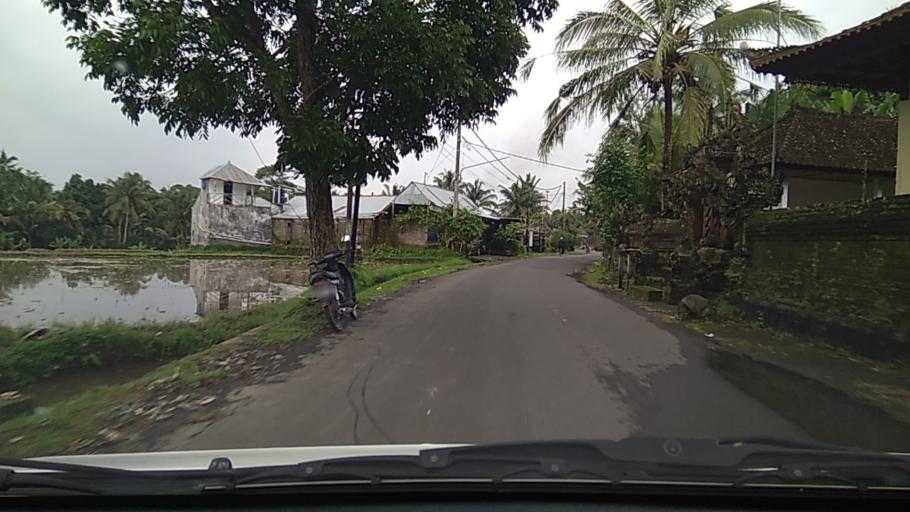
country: ID
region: Bali
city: Banjar Dujung Kaja
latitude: -8.4131
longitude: 115.2943
